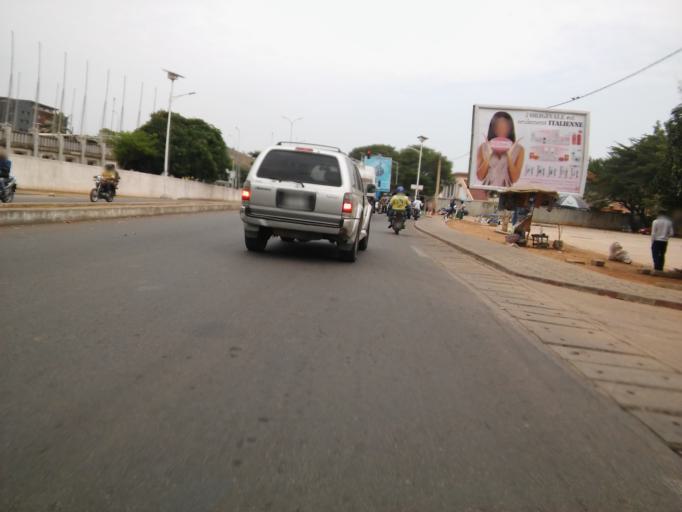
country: BJ
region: Littoral
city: Cotonou
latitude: 6.3534
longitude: 2.4045
